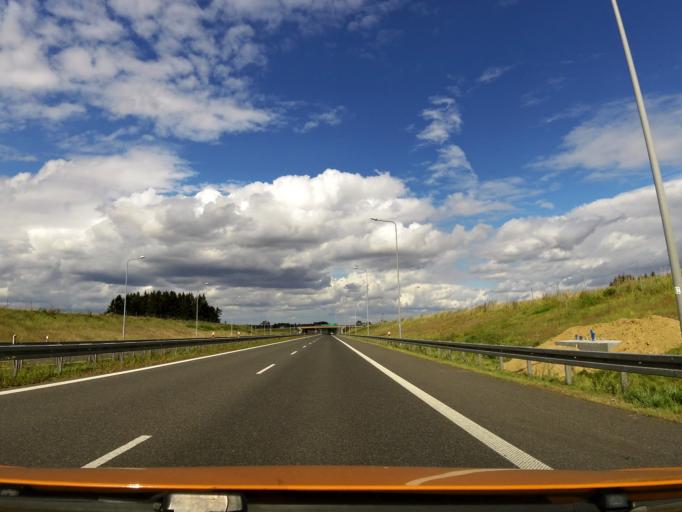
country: PL
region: West Pomeranian Voivodeship
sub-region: Powiat goleniowski
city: Nowogard
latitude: 53.6814
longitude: 15.0861
